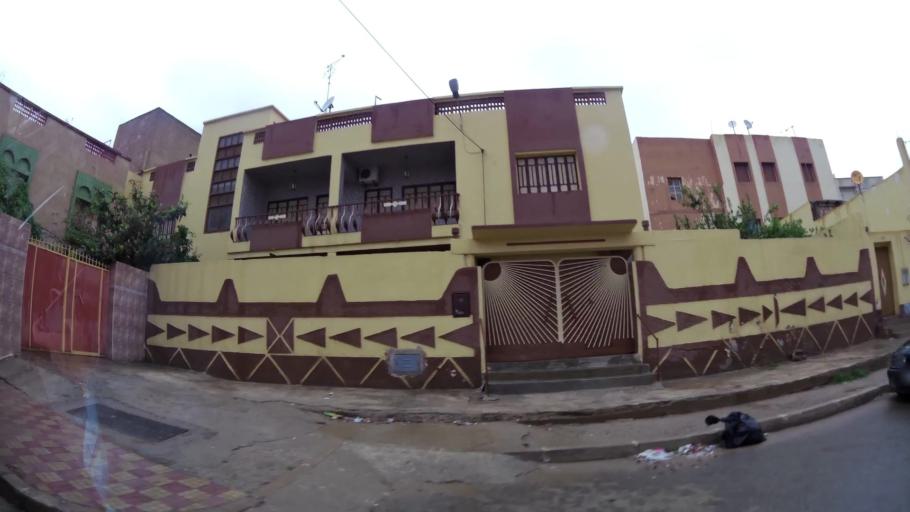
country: MA
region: Oriental
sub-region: Nador
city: Nador
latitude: 35.1742
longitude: -2.9397
